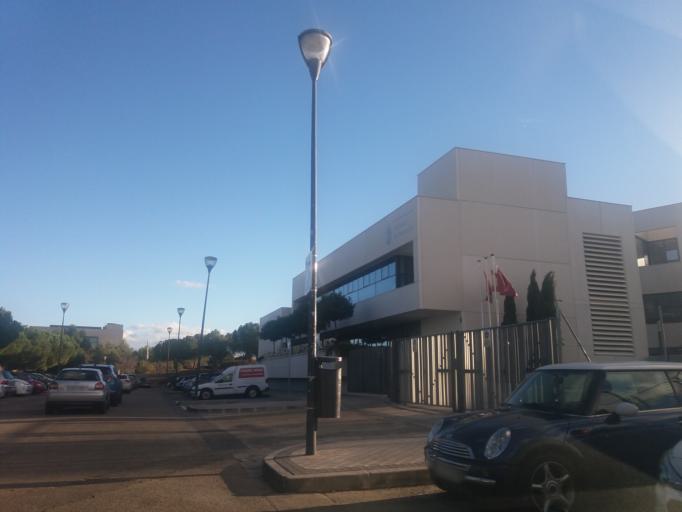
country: ES
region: Madrid
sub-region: Provincia de Madrid
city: Pozuelo de Alarcon
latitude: 40.4364
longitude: -3.8004
